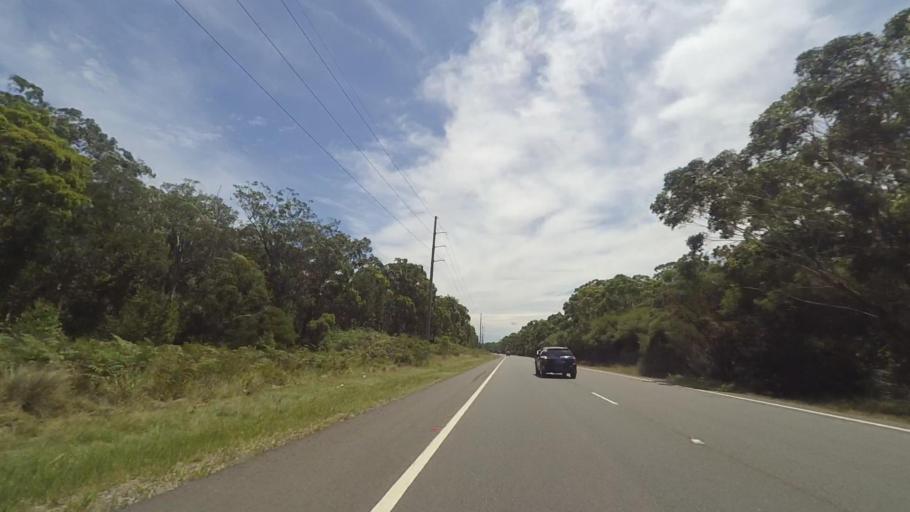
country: AU
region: New South Wales
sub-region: Port Stephens Shire
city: Anna Bay
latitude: -32.7804
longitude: 151.9938
